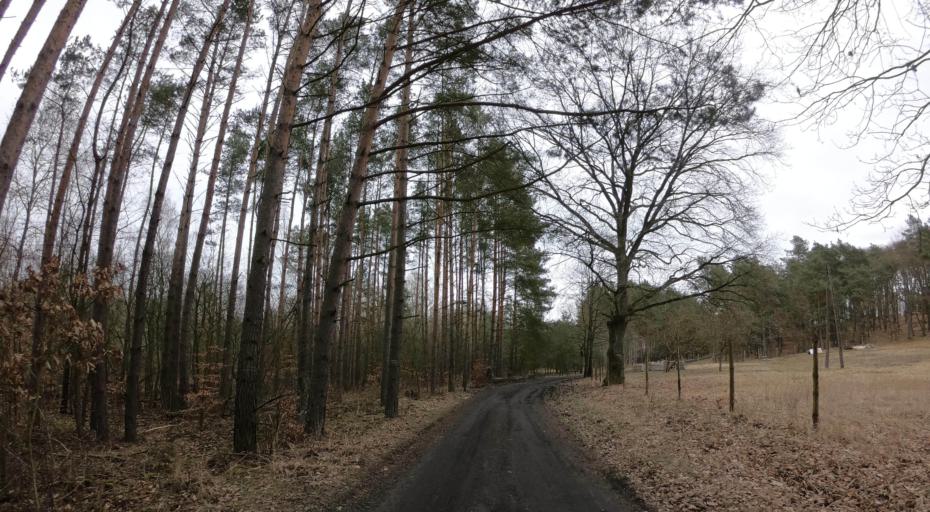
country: PL
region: West Pomeranian Voivodeship
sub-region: Powiat goleniowski
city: Stepnica
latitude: 53.6631
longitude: 14.4893
